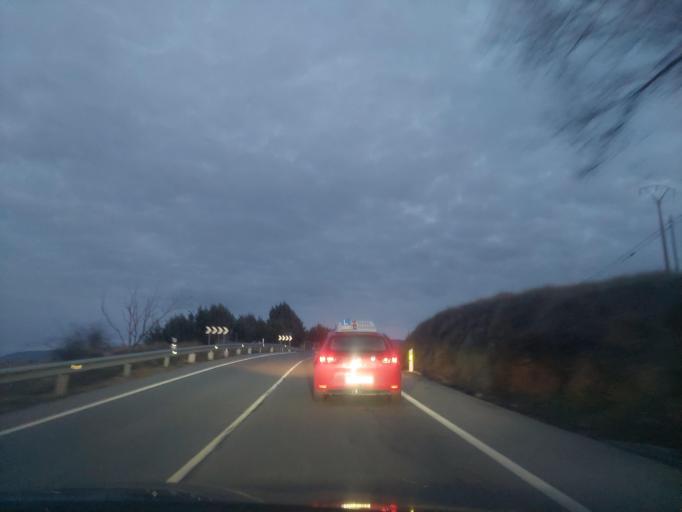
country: ES
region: Castille and Leon
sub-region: Provincia de Segovia
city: La Lastrilla
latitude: 40.9528
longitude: -4.1031
